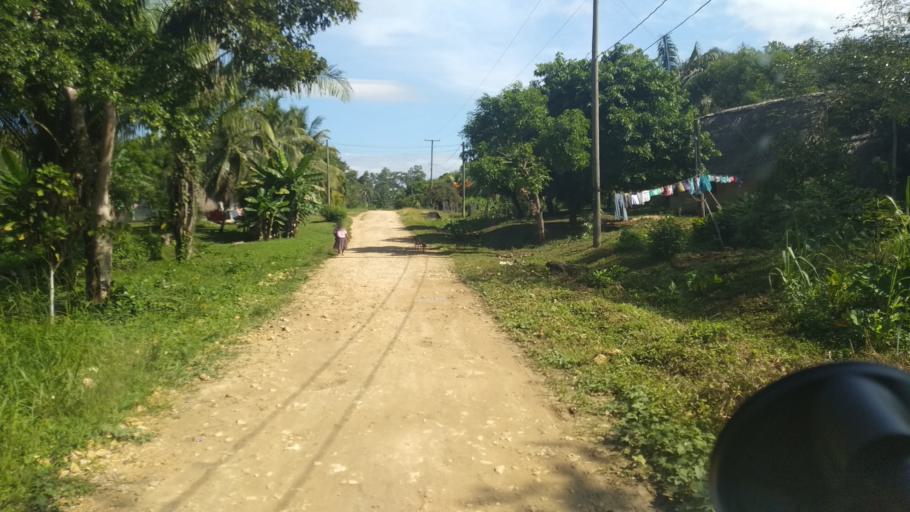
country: BZ
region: Toledo
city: Punta Gorda
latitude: 16.2167
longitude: -88.9033
